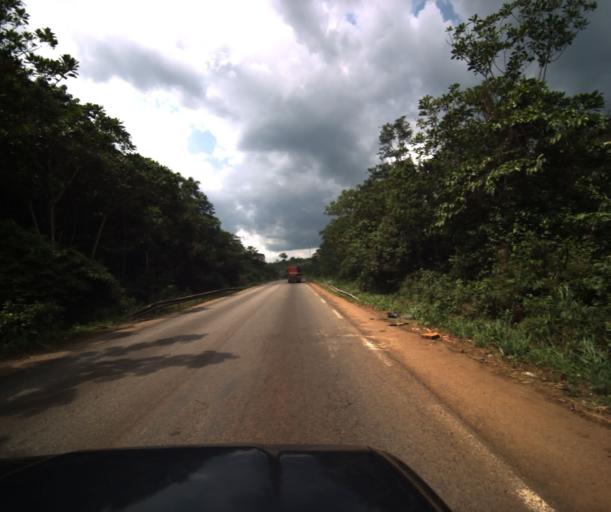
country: CM
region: Littoral
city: Edea
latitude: 3.8914
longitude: 10.0657
